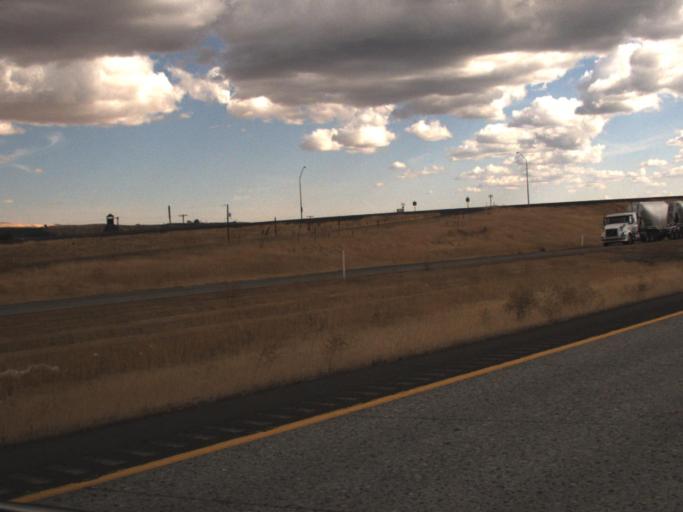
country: US
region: Washington
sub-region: Yakima County
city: Wapato
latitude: 46.4730
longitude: -120.3990
